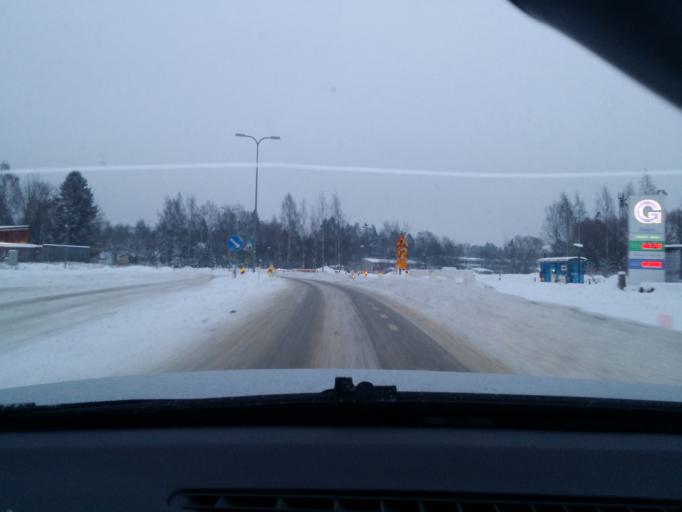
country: FI
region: Uusimaa
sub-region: Helsinki
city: Teekkarikylae
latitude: 60.2172
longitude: 24.8342
